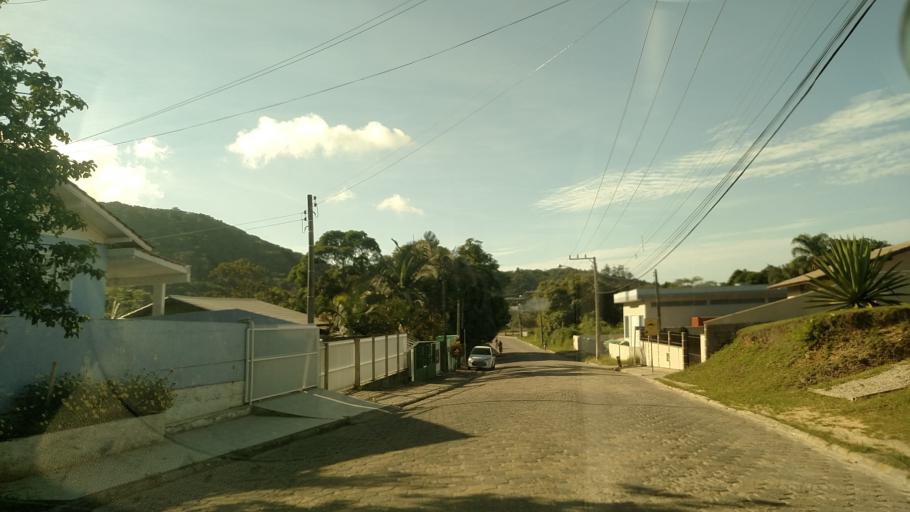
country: BR
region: Santa Catarina
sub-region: Porto Belo
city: Porto Belo
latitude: -27.1699
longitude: -48.5245
